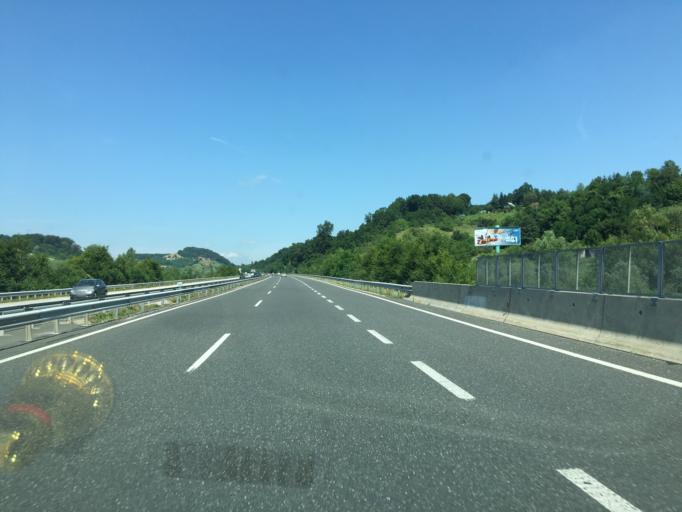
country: SI
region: Sentilj
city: Sentilj v Slov. Goricah
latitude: 46.6515
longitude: 15.6488
